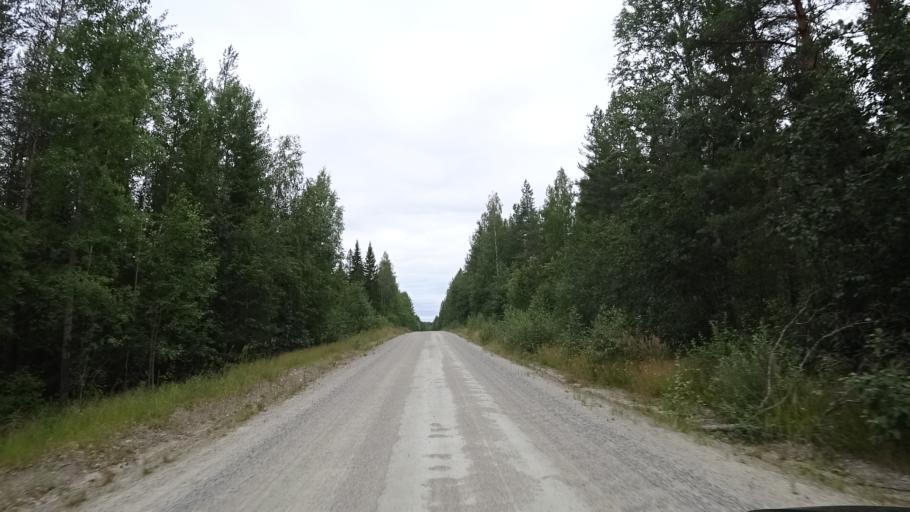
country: FI
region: North Karelia
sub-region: Joensuu
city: Eno
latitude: 63.1550
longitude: 30.6069
